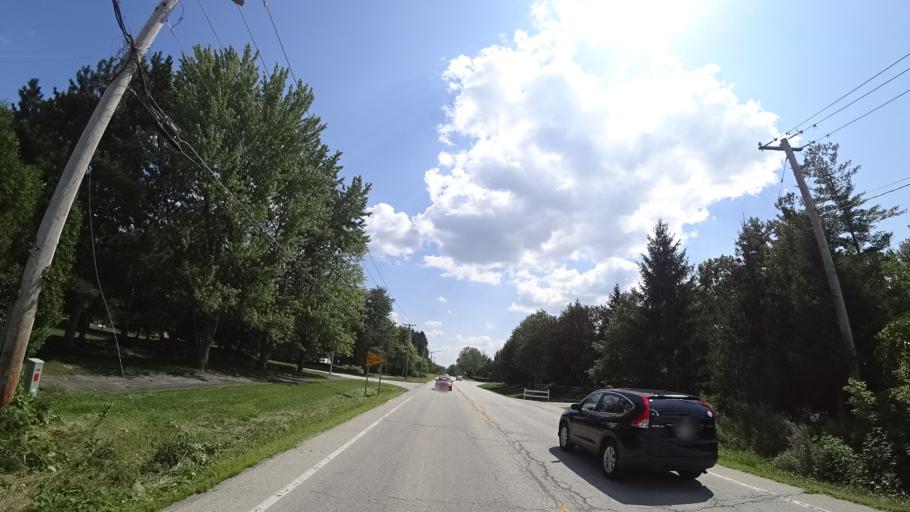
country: US
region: Illinois
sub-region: Cook County
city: Orland Park
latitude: 41.6275
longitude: -87.8195
